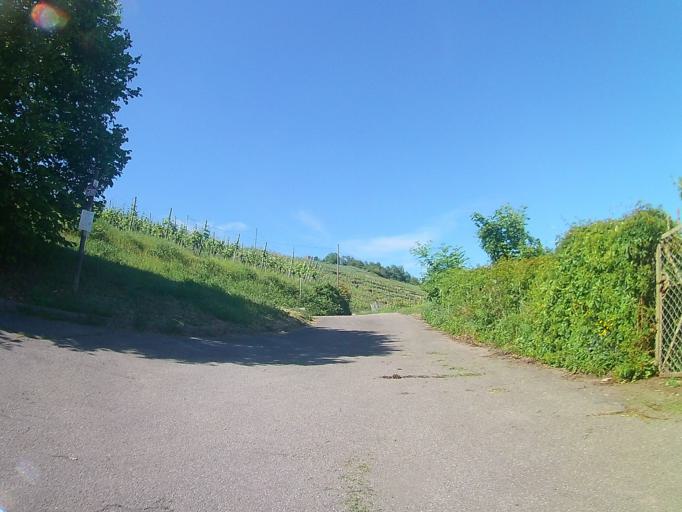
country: DE
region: Baden-Wuerttemberg
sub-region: Regierungsbezirk Stuttgart
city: Fellbach
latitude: 48.7683
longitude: 9.2691
